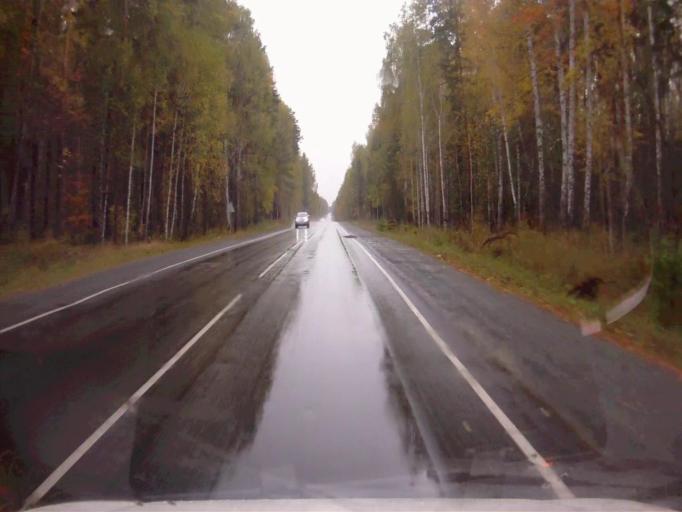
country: RU
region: Chelyabinsk
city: Tayginka
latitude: 55.5770
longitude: 60.6456
